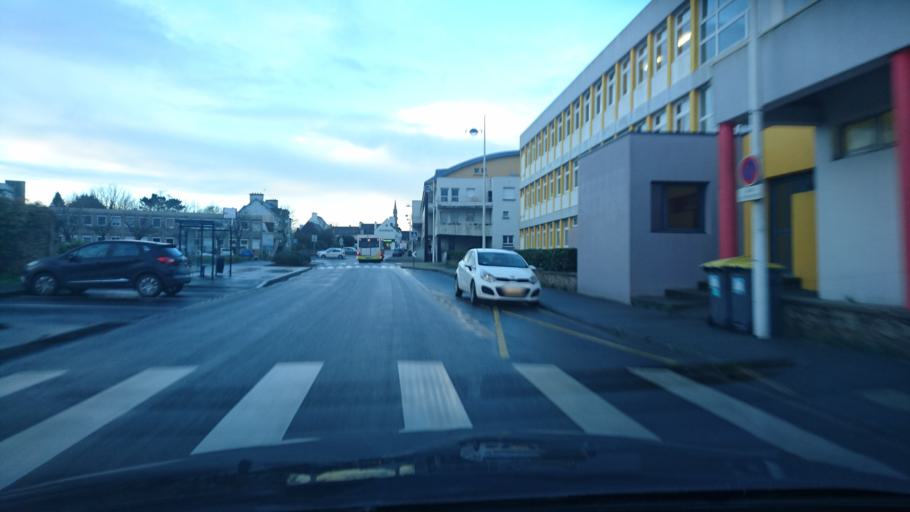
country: FR
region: Brittany
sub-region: Departement du Finistere
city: Guilers
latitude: 48.4228
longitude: -4.5585
